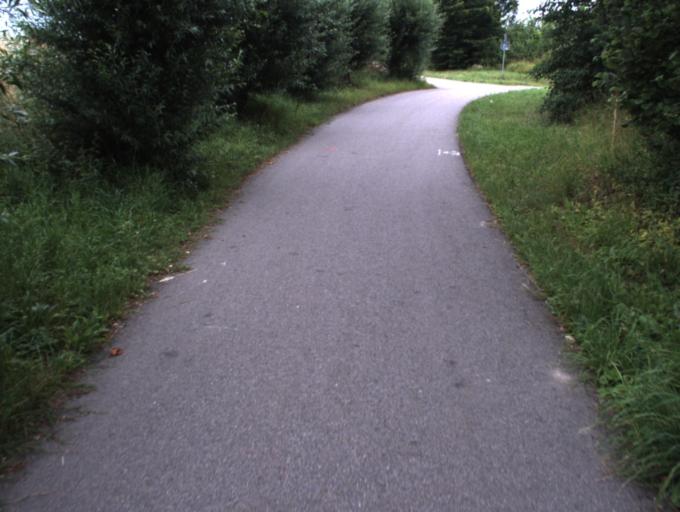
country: SE
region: Skane
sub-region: Helsingborg
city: Odakra
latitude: 56.0764
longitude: 12.7369
